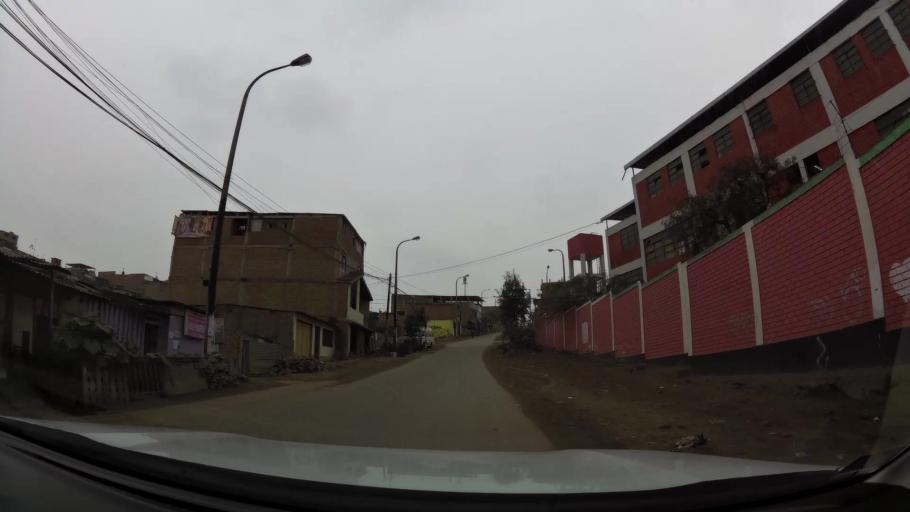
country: PE
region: Lima
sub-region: Lima
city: Surco
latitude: -12.2206
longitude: -76.9178
